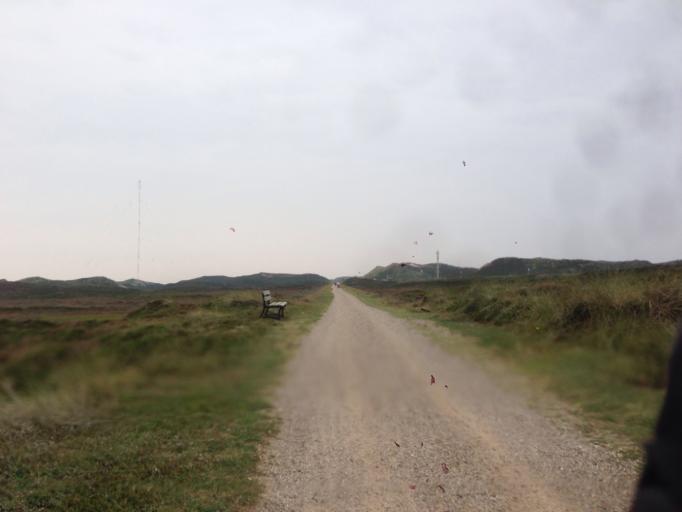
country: DE
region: Schleswig-Holstein
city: Westerland
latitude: 54.8191
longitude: 8.2931
